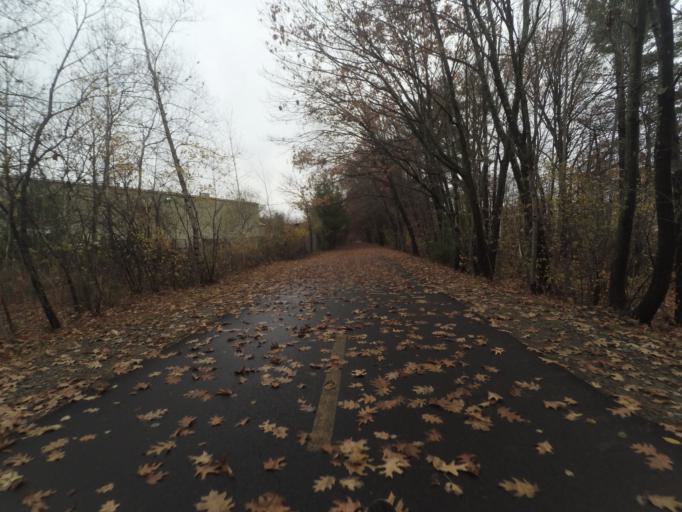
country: US
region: Massachusetts
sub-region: Middlesex County
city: Bedford
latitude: 42.4792
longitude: -71.2672
